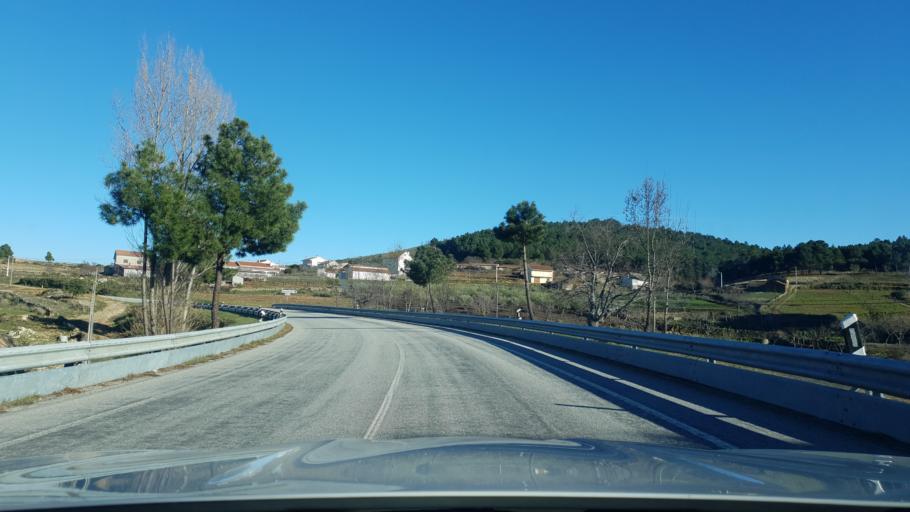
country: PT
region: Braganca
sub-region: Freixo de Espada A Cinta
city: Freixo de Espada a Cinta
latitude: 41.1789
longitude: -6.8129
